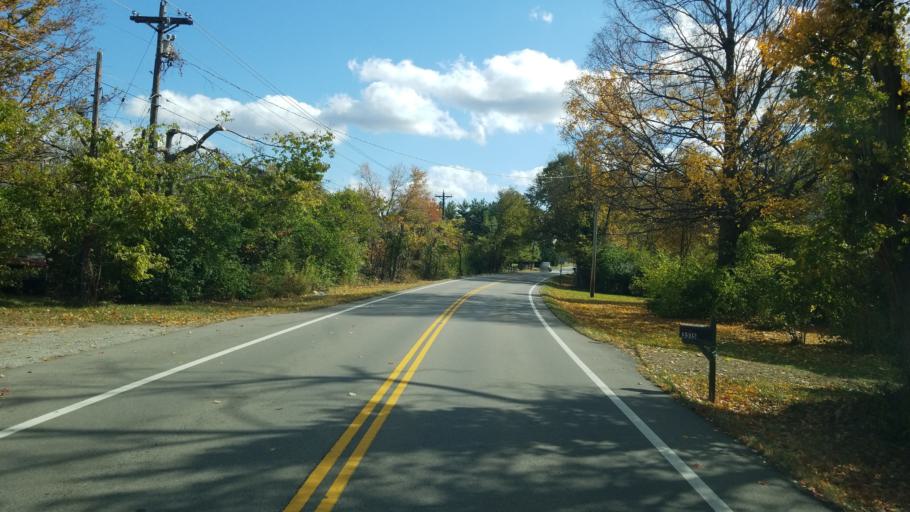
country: US
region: Ohio
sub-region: Warren County
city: Morrow
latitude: 39.4100
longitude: -84.1428
